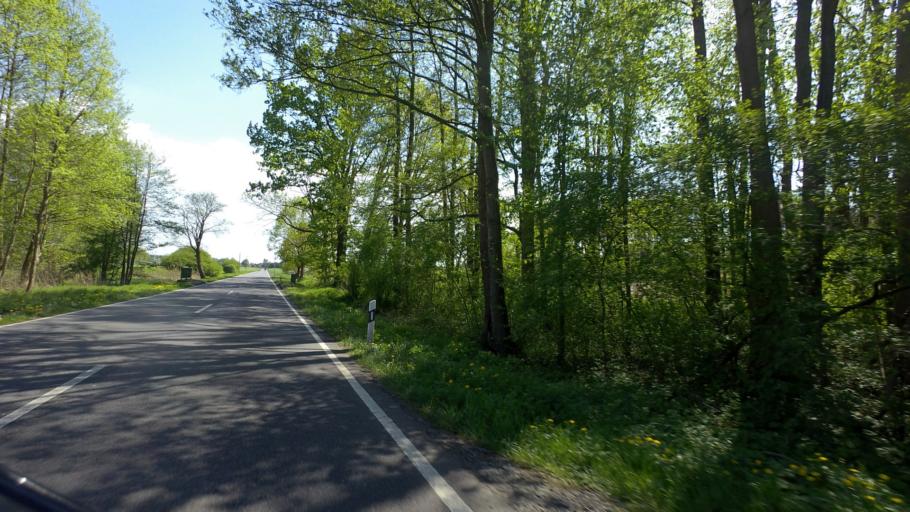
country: DE
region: Brandenburg
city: Lieberose
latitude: 51.9889
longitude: 14.2092
